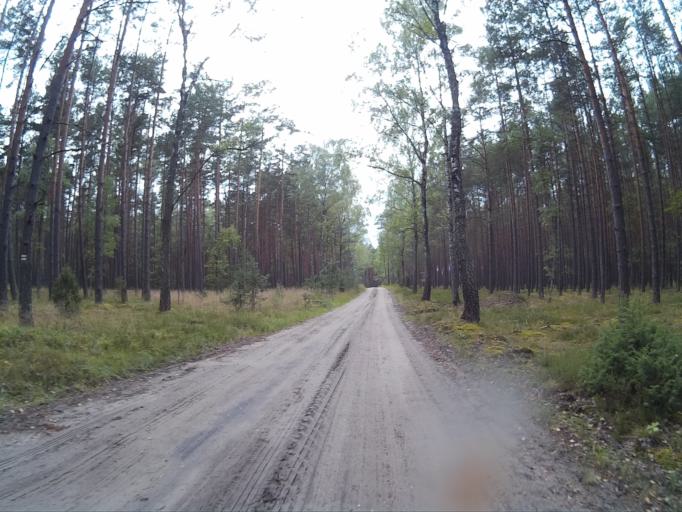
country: PL
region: Kujawsko-Pomorskie
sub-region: Powiat tucholski
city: Sliwice
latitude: 53.6652
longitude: 18.2608
